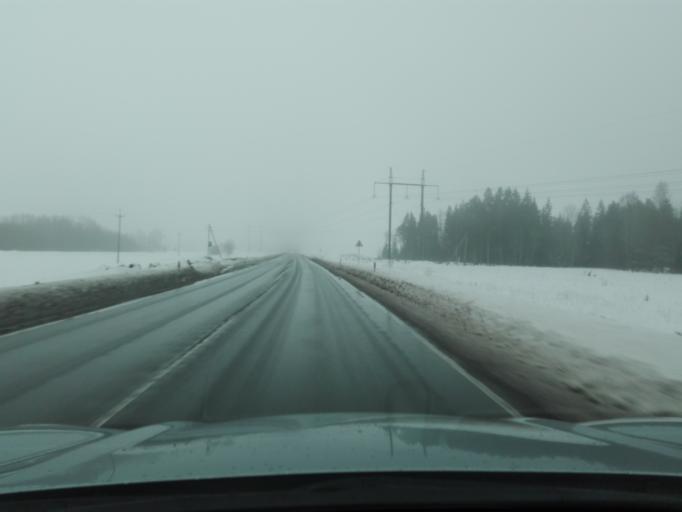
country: EE
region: Raplamaa
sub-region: Kohila vald
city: Kohila
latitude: 59.2152
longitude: 24.7764
